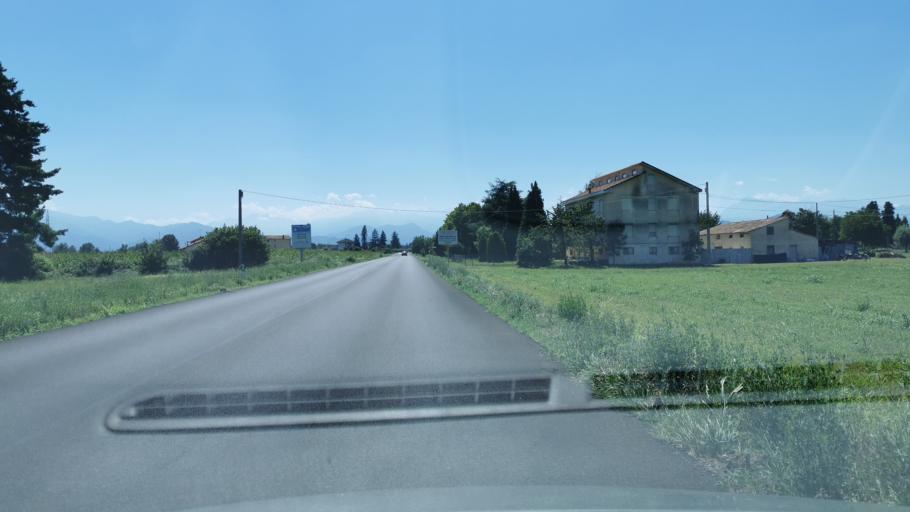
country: IT
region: Piedmont
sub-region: Provincia di Cuneo
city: Roata Rossi
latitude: 44.4369
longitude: 7.5618
